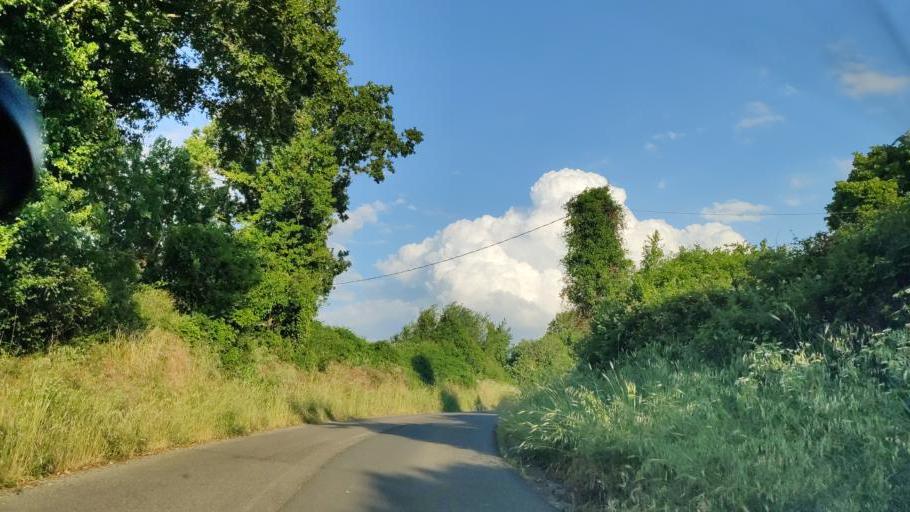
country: IT
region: Umbria
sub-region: Provincia di Terni
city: Lugnano in Teverina
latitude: 42.5854
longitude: 12.3821
